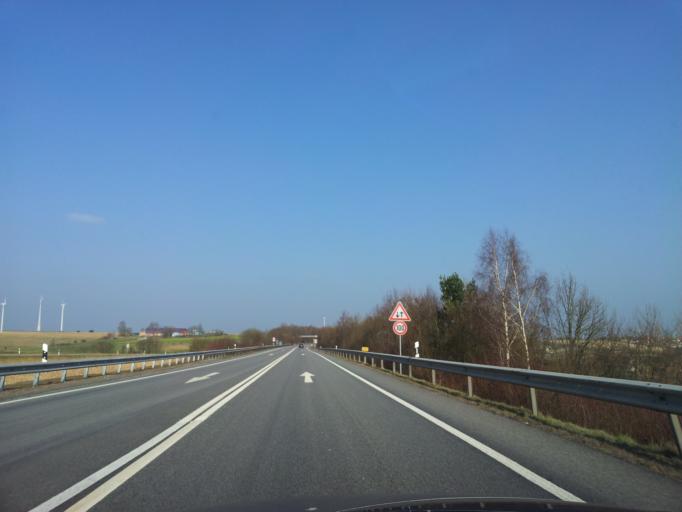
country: DE
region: Rheinland-Pfalz
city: Hermersberg
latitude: 49.3057
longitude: 7.6197
